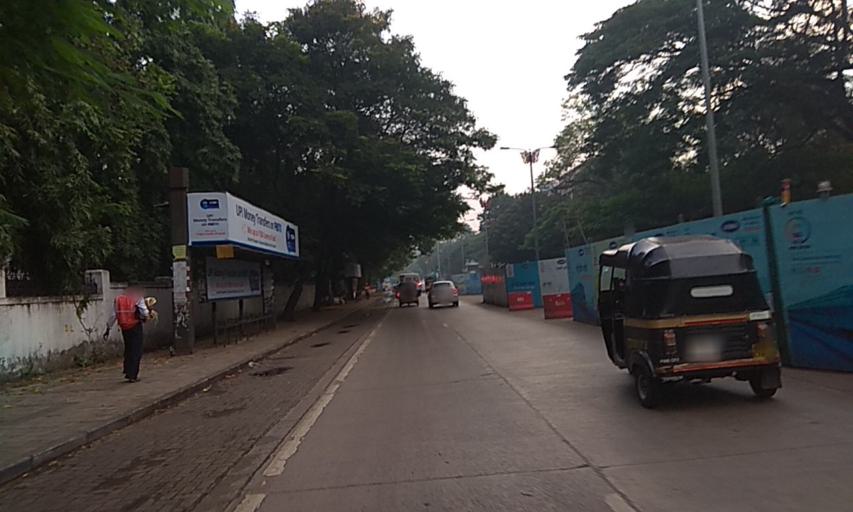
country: IN
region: Maharashtra
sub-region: Pune Division
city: Shivaji Nagar
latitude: 18.5388
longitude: 73.8822
